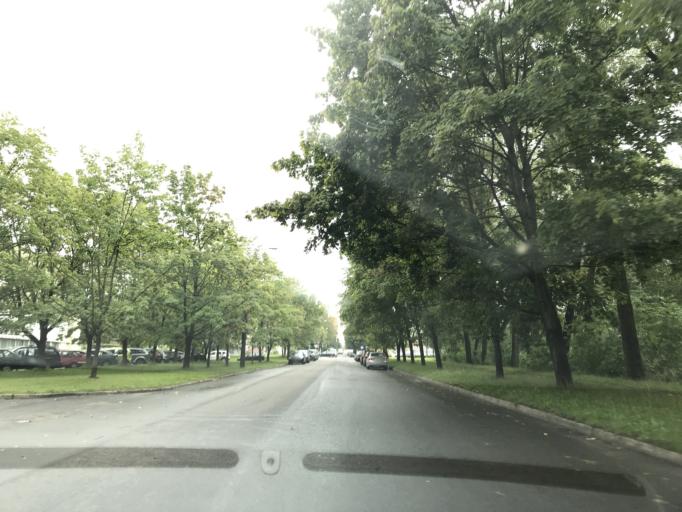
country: BY
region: Minsk
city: Minsk
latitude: 53.9450
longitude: 27.6196
